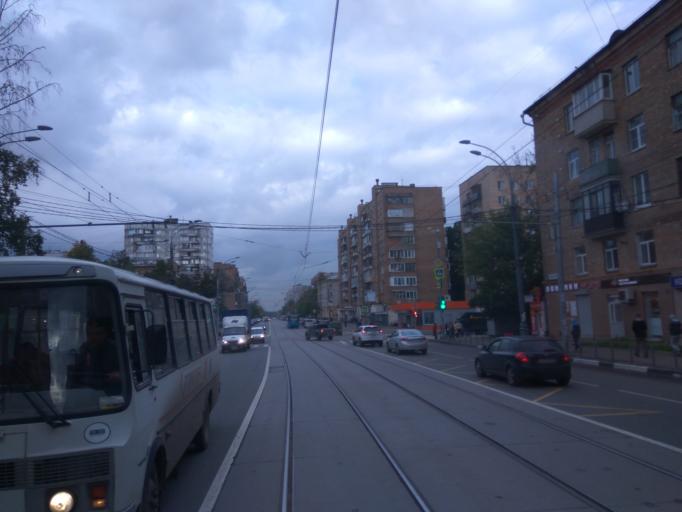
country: RU
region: Moskovskaya
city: Izmaylovo
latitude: 55.7932
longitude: 37.7986
